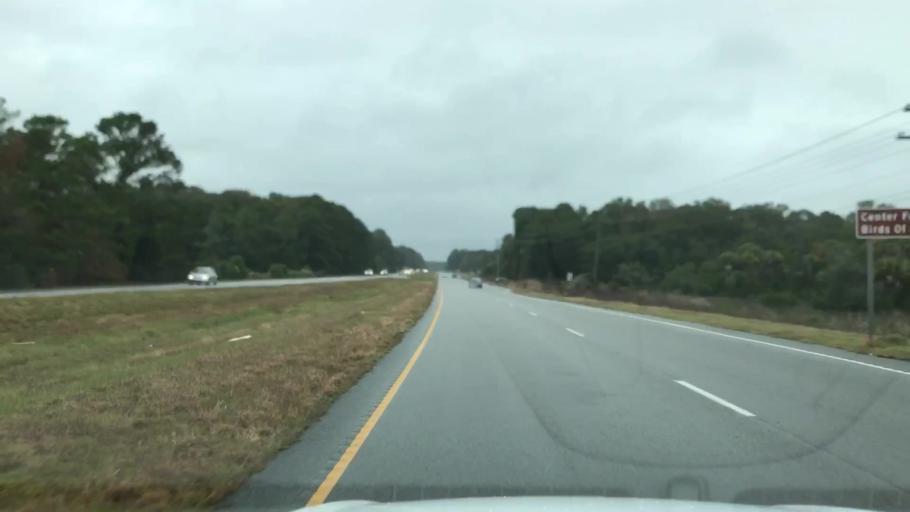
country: US
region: South Carolina
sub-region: Charleston County
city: Isle of Palms
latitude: 32.9201
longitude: -79.7159
